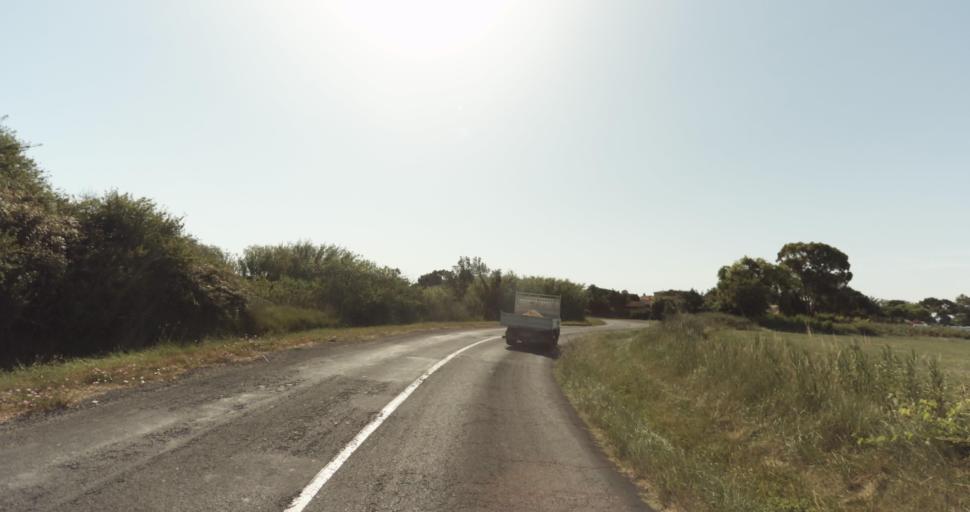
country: FR
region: Languedoc-Roussillon
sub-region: Departement des Pyrenees-Orientales
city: Saint-Cyprien-Plage
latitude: 42.6362
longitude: 3.0095
